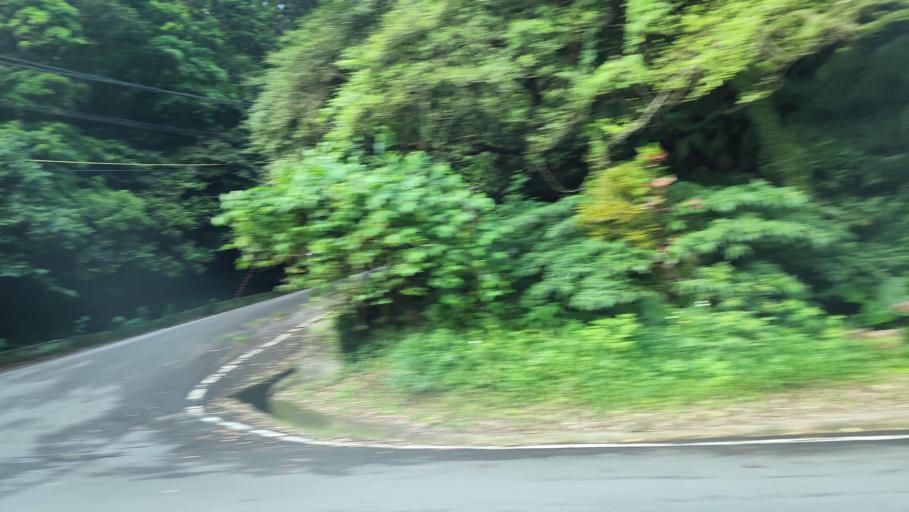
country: TW
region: Taiwan
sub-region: Keelung
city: Keelung
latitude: 25.1707
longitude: 121.6596
